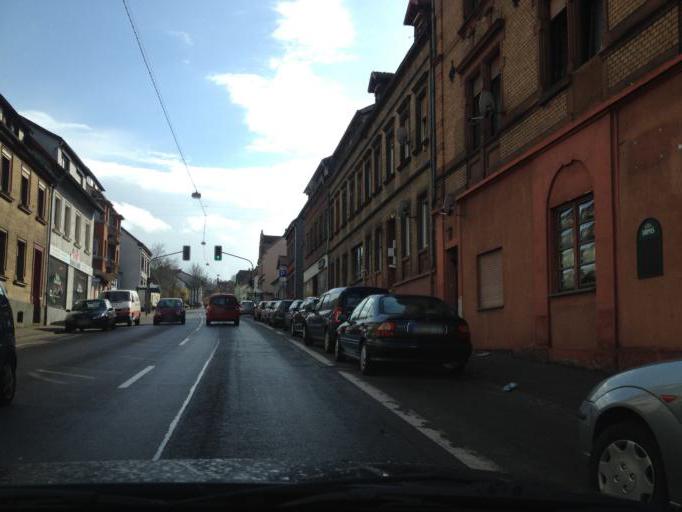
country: DE
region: Saarland
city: Neunkirchen
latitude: 49.3672
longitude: 7.1861
